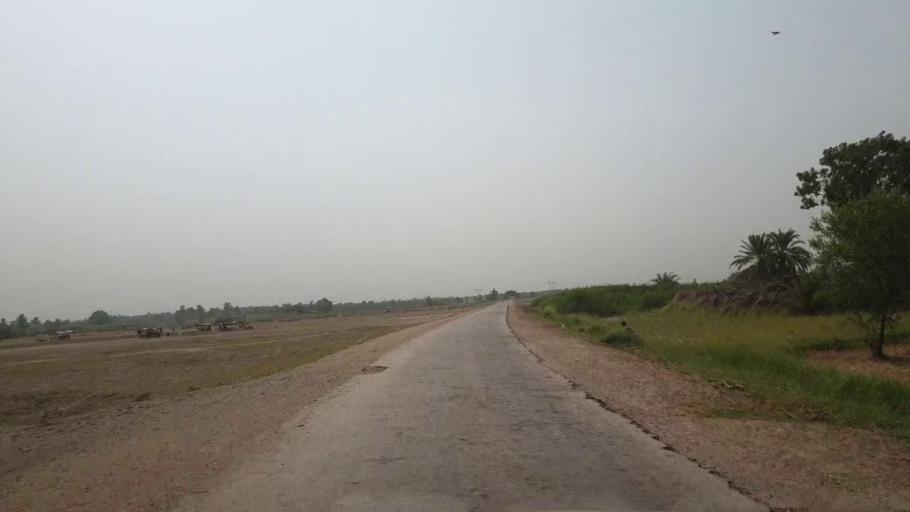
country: PK
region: Sindh
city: Gambat
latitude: 27.4236
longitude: 68.5433
